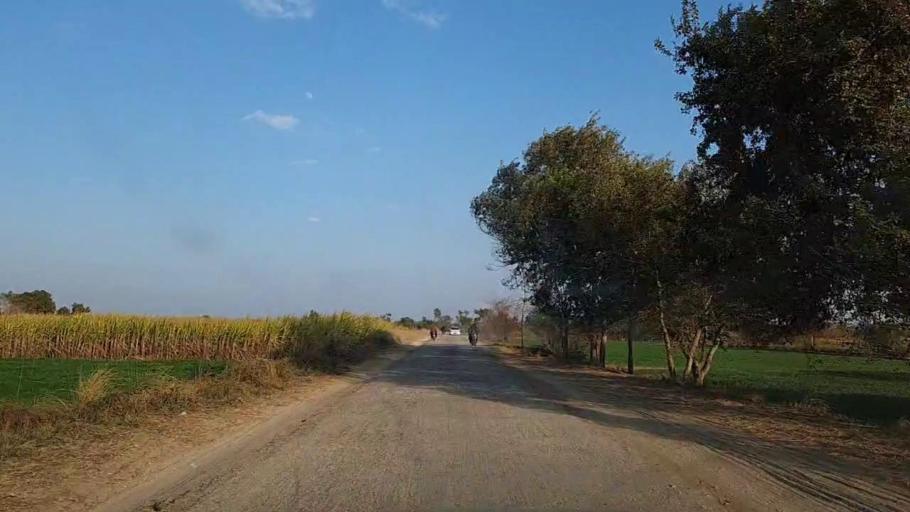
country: PK
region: Sindh
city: Sanghar
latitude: 26.2643
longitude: 68.9584
